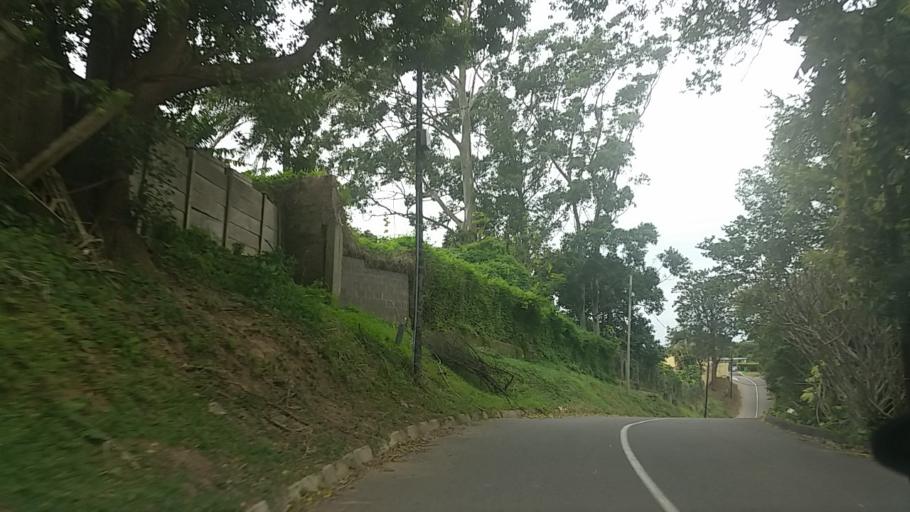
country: ZA
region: KwaZulu-Natal
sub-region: eThekwini Metropolitan Municipality
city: Berea
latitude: -29.8394
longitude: 30.9365
